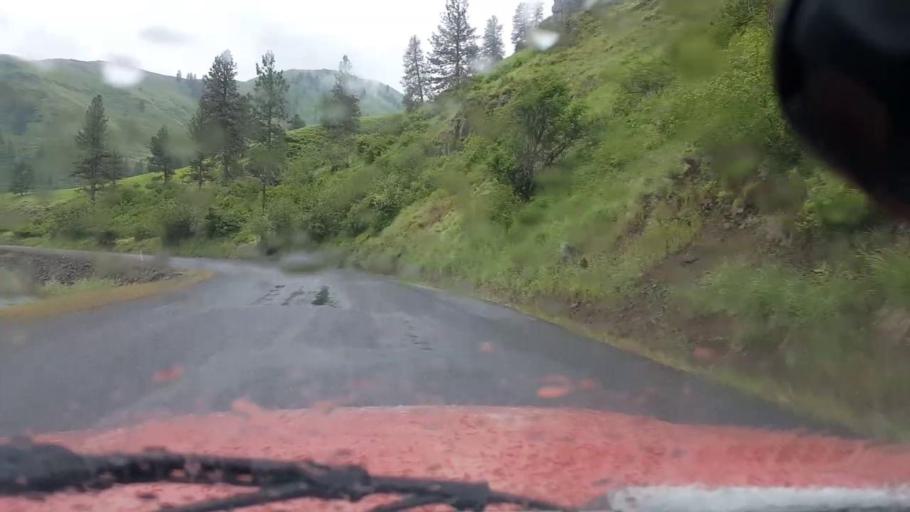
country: US
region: Washington
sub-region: Asotin County
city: Asotin
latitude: 46.0318
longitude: -117.3283
